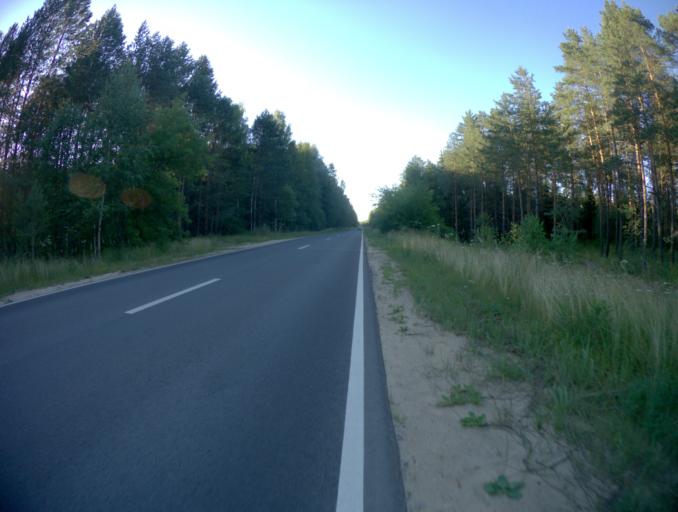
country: RU
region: Vladimir
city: Galitsy
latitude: 56.1188
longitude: 42.8726
